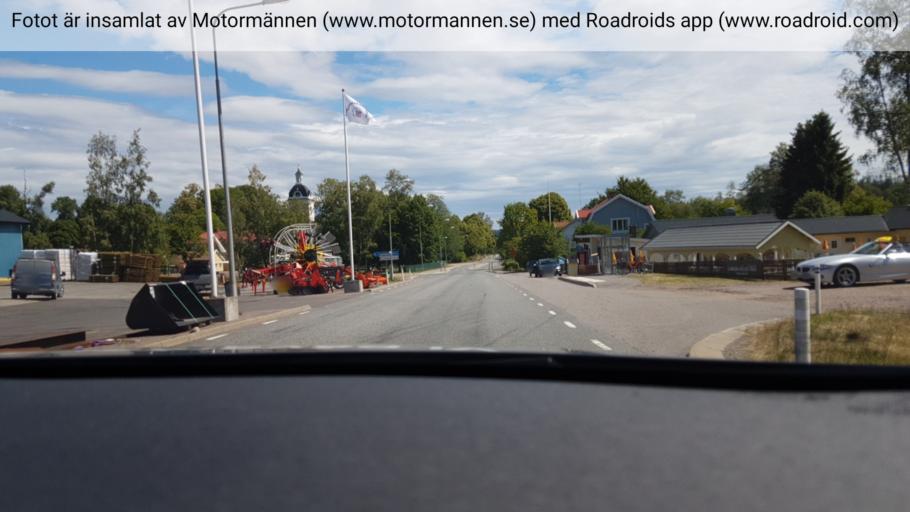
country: SE
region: Joenkoeping
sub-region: Aneby Kommun
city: Aneby
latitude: 57.9749
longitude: 14.7993
